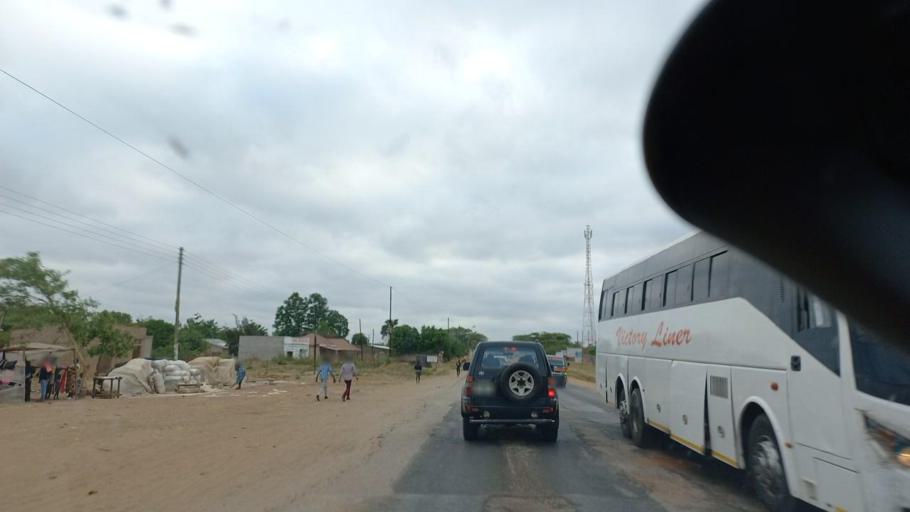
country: ZM
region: Lusaka
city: Chongwe
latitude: -15.3396
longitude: 28.6663
